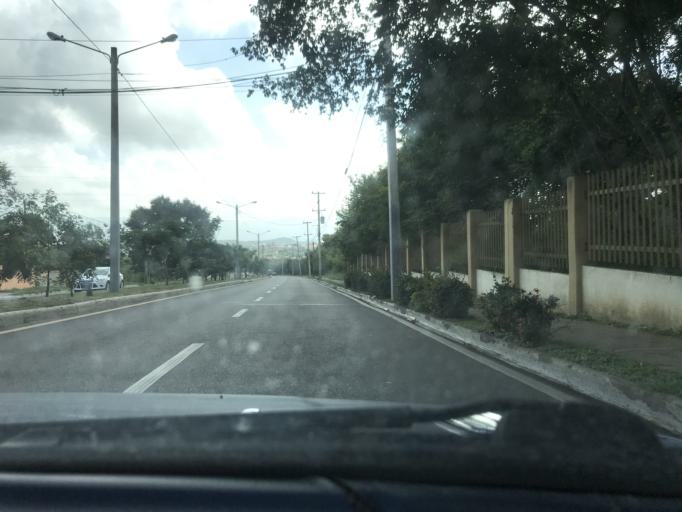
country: DO
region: Santiago
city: Santiago de los Caballeros
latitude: 19.4276
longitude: -70.7285
